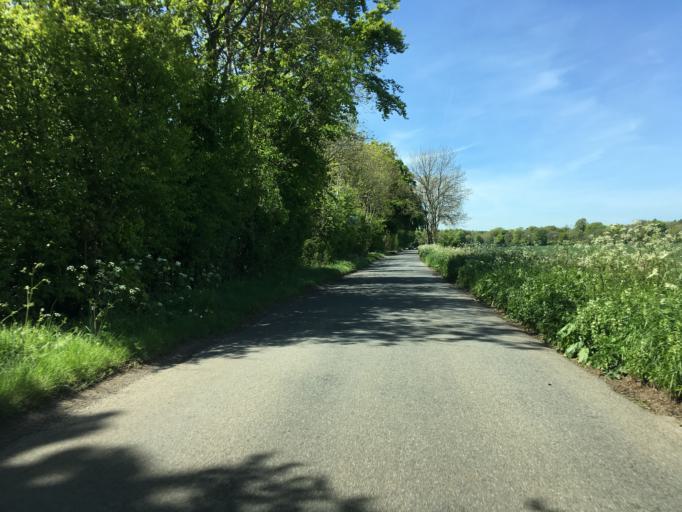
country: GB
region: England
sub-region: Gloucestershire
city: Coates
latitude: 51.7125
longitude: -2.0420
